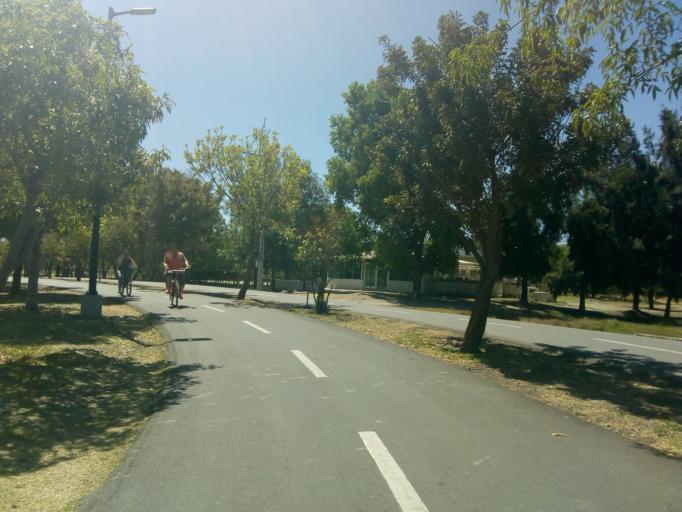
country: MX
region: Guanajuato
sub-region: Leon
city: La Ermita
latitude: 21.1868
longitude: -101.6909
